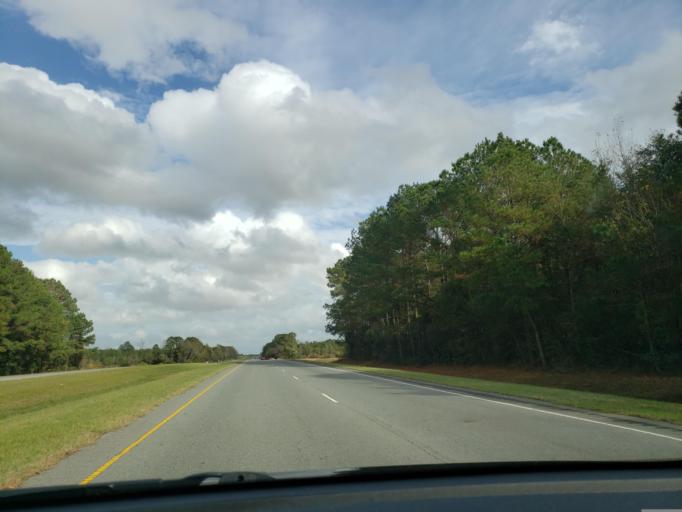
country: US
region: North Carolina
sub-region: Duplin County
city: Kenansville
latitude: 34.9313
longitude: -77.9960
